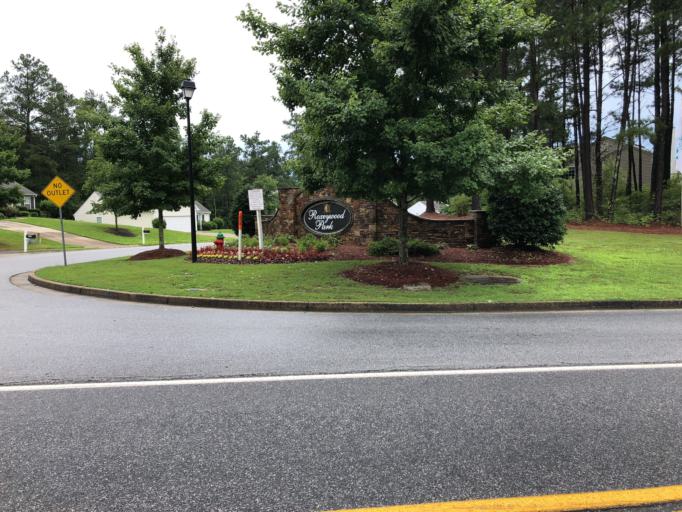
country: US
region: Georgia
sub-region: Barrow County
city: Auburn
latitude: 33.9516
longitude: -83.7969
